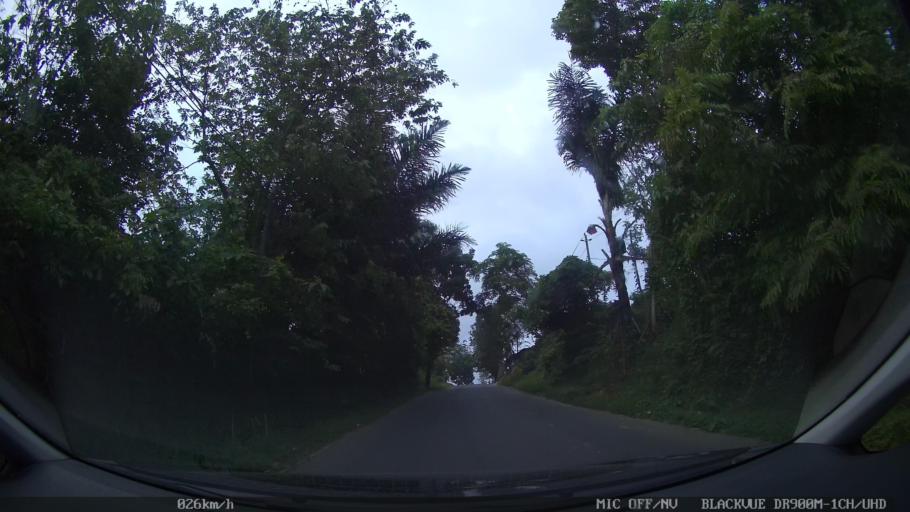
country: ID
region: Lampung
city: Bandarlampung
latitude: -5.4206
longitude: 105.2861
